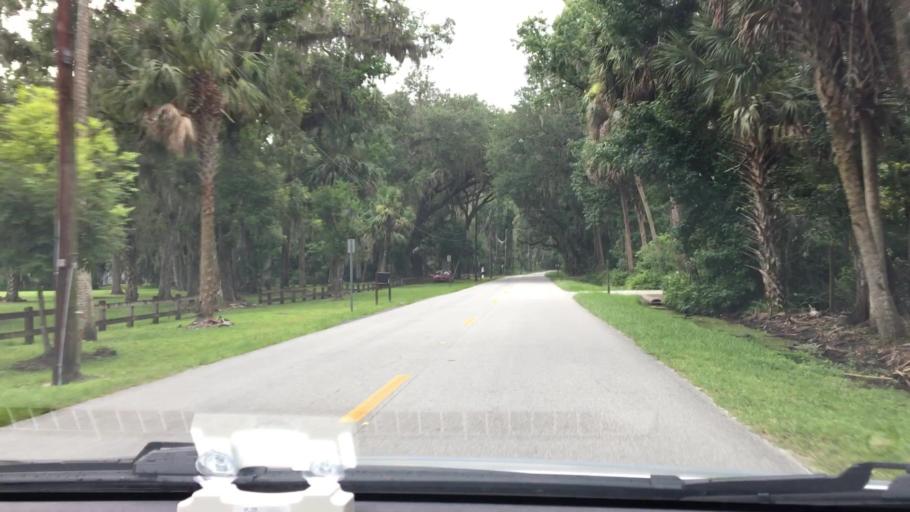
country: US
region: Florida
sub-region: Volusia County
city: Deltona
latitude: 28.8600
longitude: -81.2399
